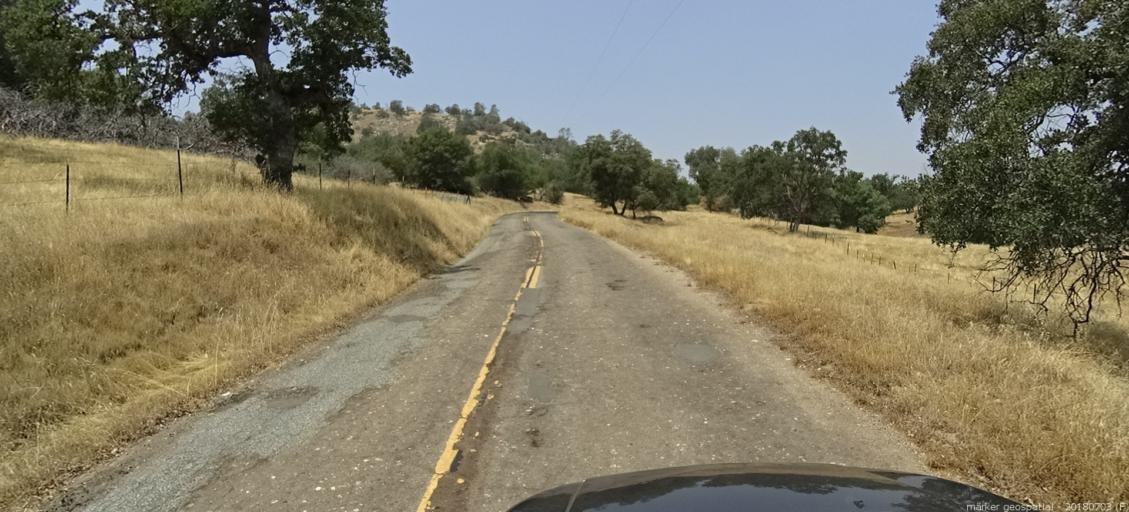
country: US
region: California
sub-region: Madera County
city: Yosemite Lakes
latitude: 37.0584
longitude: -119.6625
